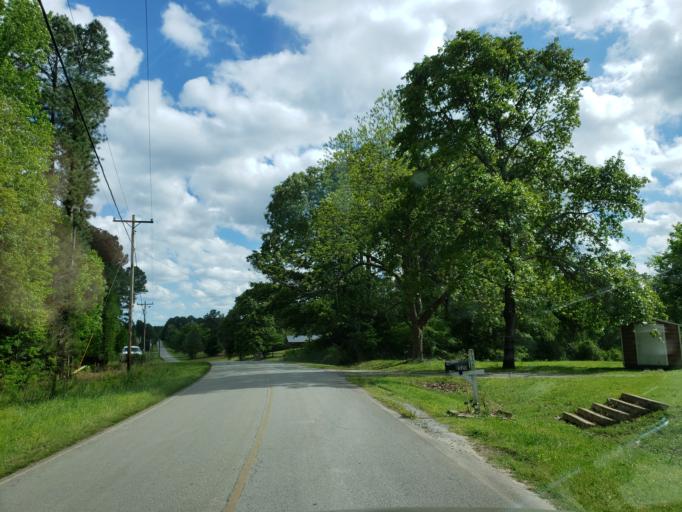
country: US
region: Georgia
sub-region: Haralson County
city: Tallapoosa
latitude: 33.6998
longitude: -85.3267
